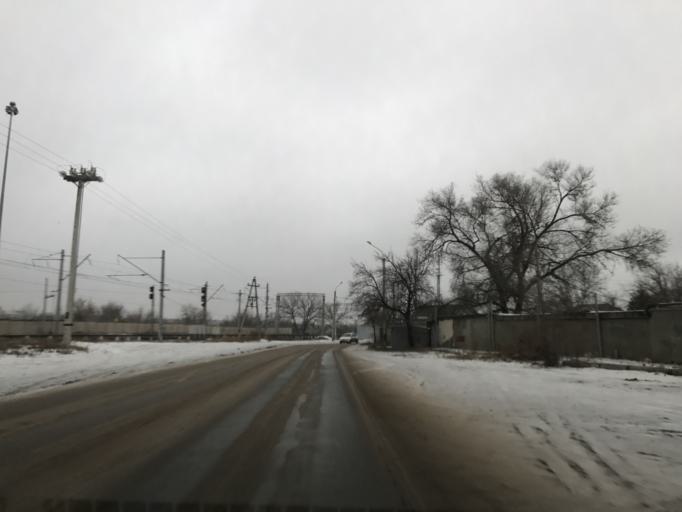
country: RU
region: Rostov
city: Kamensk-Shakhtinskiy
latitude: 48.3170
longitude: 40.2601
